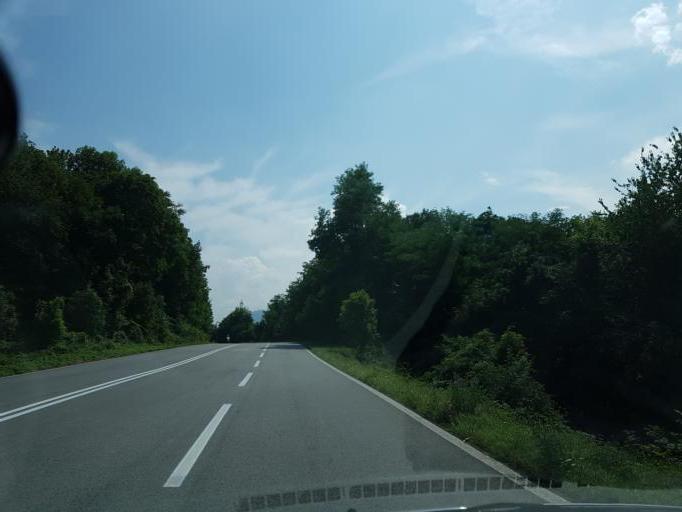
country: IT
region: Piedmont
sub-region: Provincia di Cuneo
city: Borgo San Dalmazzo
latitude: 44.3415
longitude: 7.4755
